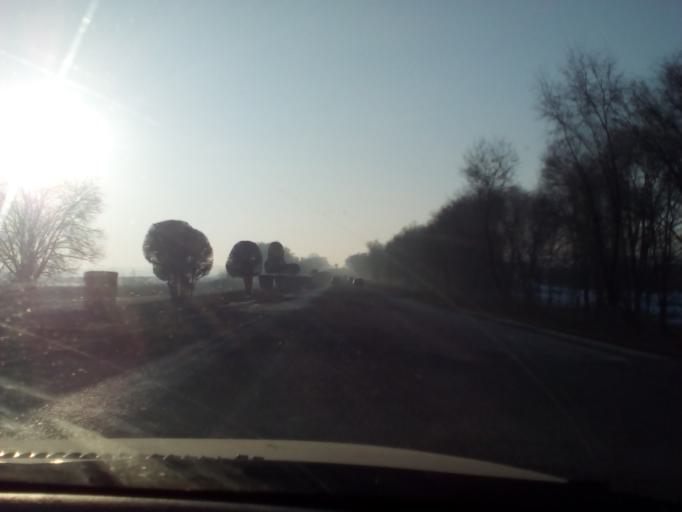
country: KZ
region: Almaty Oblysy
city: Burunday
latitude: 43.2231
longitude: 76.5869
